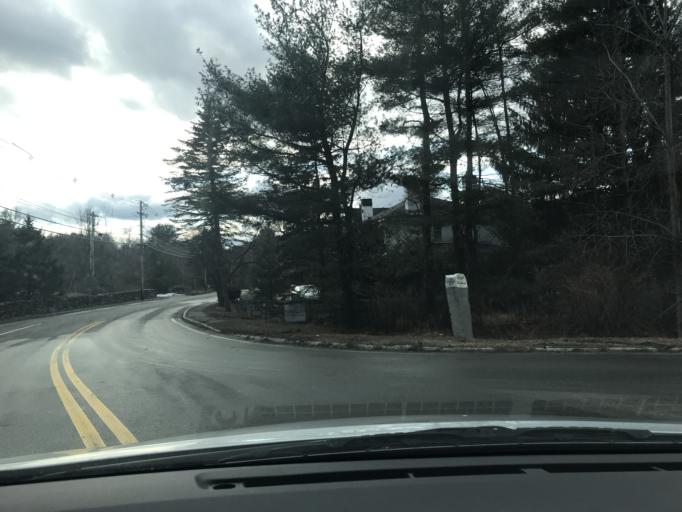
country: US
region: Massachusetts
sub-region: Worcester County
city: Harvard
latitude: 42.4881
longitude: -71.5488
